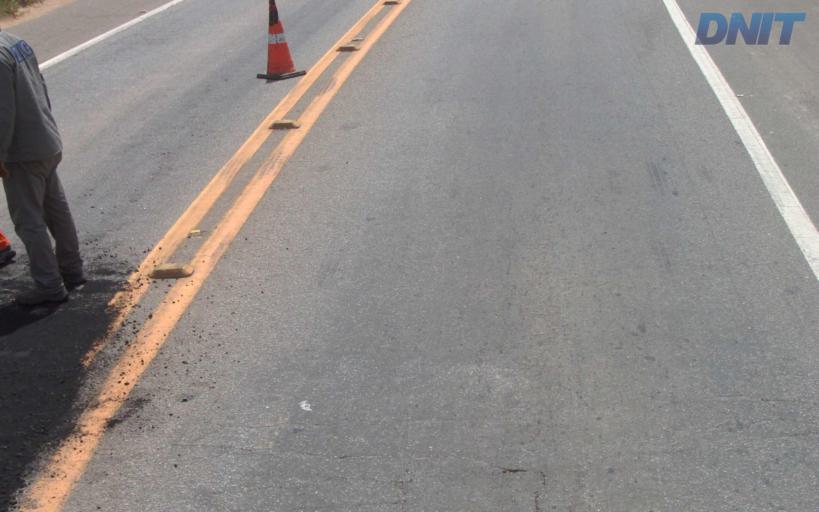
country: BR
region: Minas Gerais
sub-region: Governador Valadares
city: Governador Valadares
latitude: -18.8872
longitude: -42.0038
